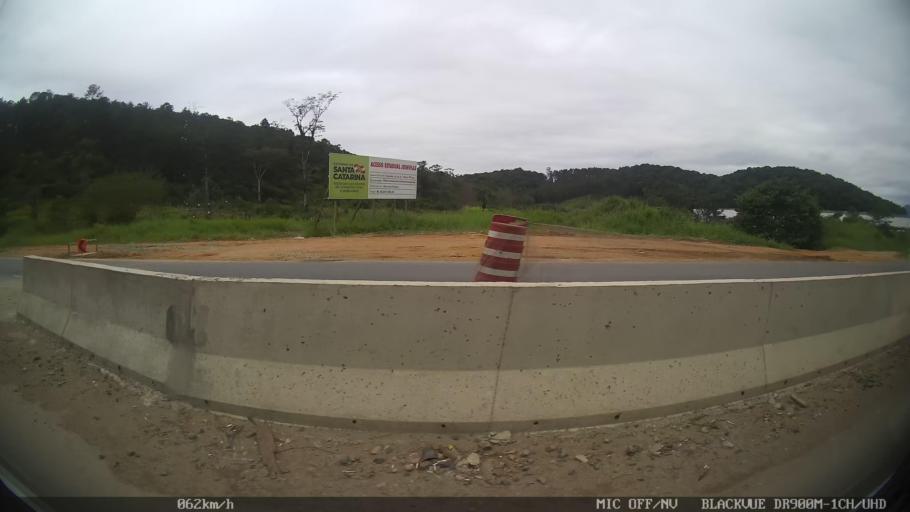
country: BR
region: Santa Catarina
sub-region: Joinville
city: Joinville
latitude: -26.2572
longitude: -48.8981
